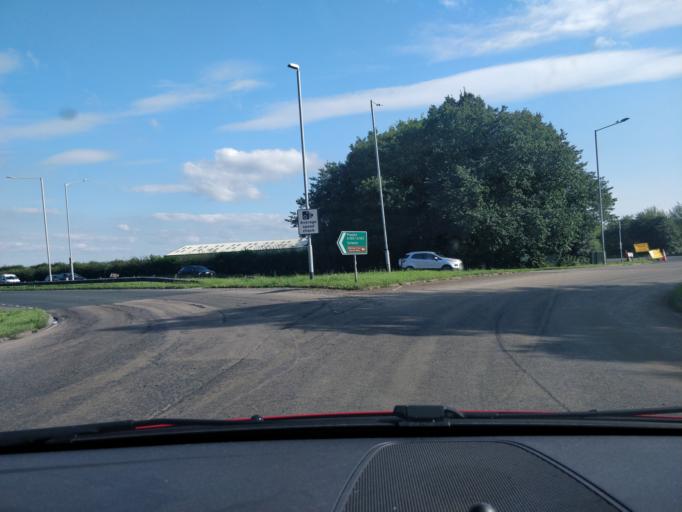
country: GB
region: England
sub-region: Lancashire
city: Banks
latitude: 53.6733
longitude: -2.9218
